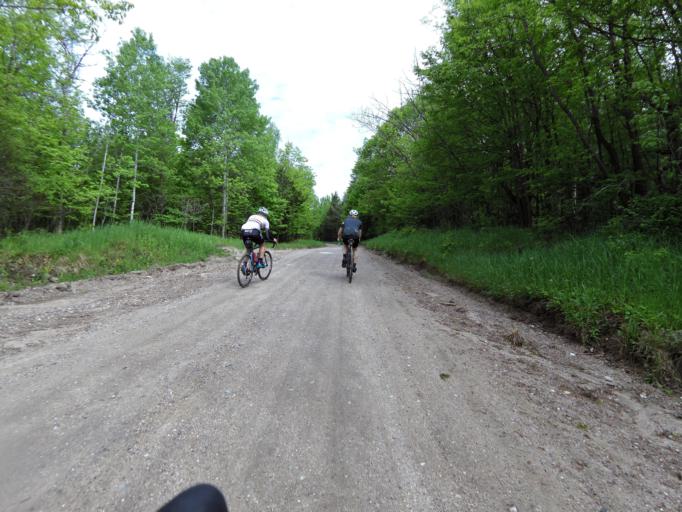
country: CA
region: Quebec
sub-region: Outaouais
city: Wakefield
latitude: 45.7615
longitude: -75.9154
